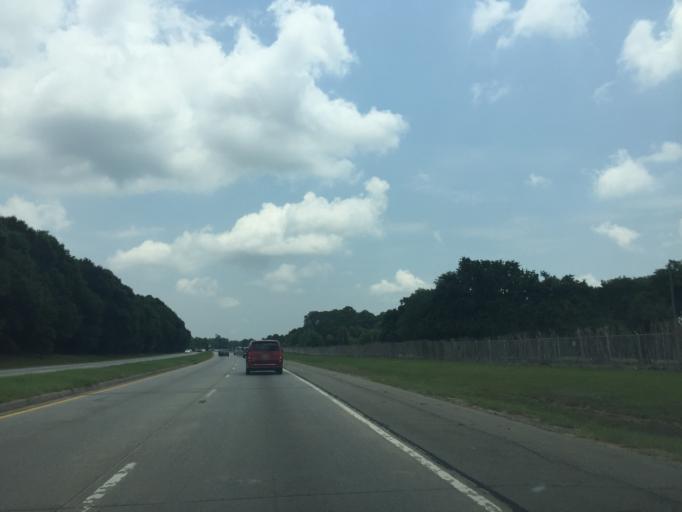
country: US
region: Georgia
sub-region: Chatham County
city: Savannah
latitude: 32.0332
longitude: -81.1281
